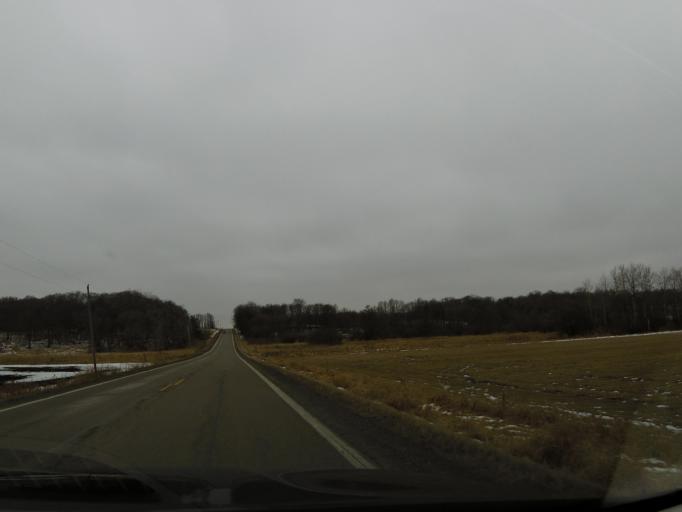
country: US
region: Minnesota
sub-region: Carver County
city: Watertown
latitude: 45.0007
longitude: -93.8488
